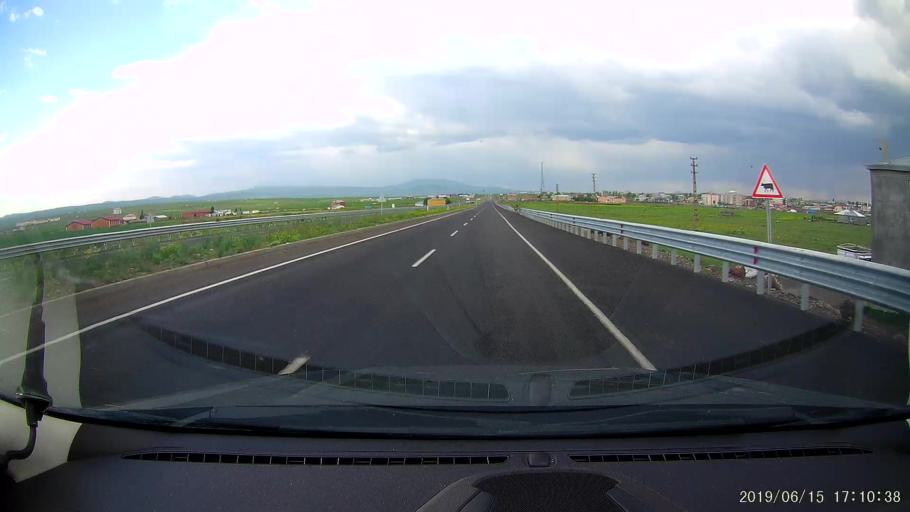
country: TR
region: Kars
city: Kars
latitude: 40.6201
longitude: 43.1336
